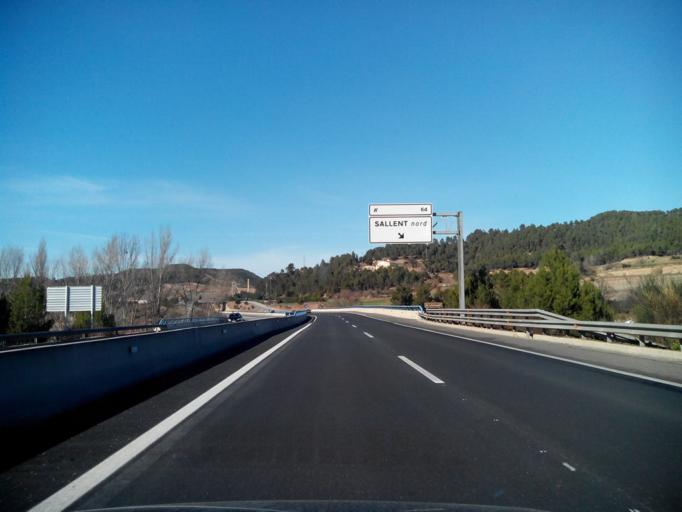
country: ES
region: Catalonia
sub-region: Provincia de Barcelona
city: Sallent
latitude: 41.8294
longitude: 1.8857
